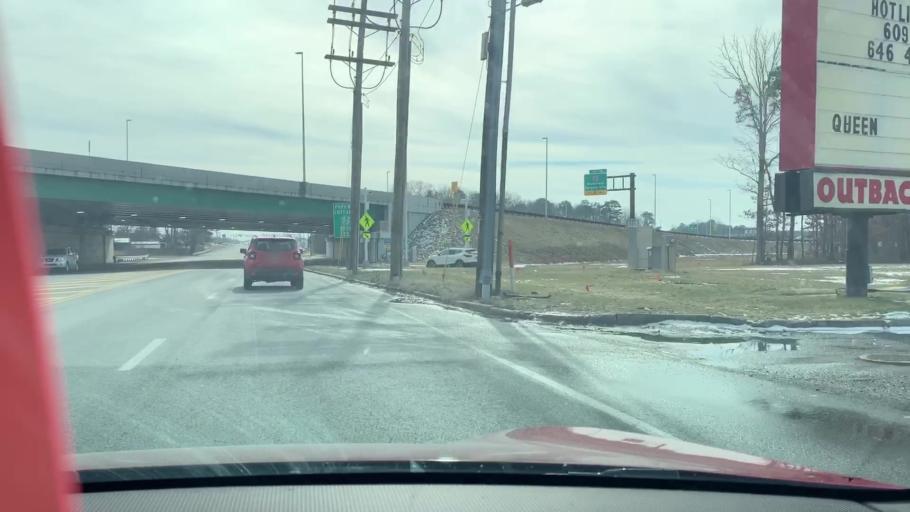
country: US
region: New Jersey
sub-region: Atlantic County
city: Northfield
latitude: 39.3992
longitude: -74.5612
